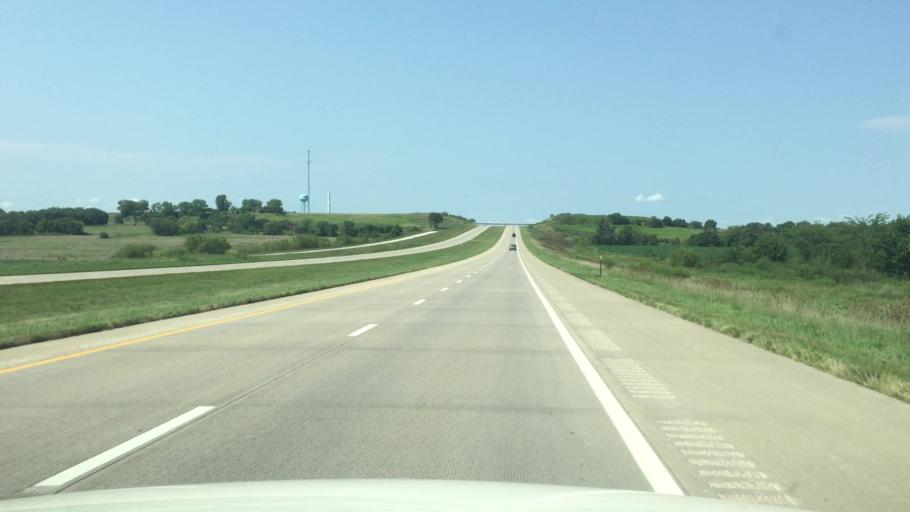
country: US
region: Kansas
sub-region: Linn County
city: Pleasanton
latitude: 38.0973
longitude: -94.7133
